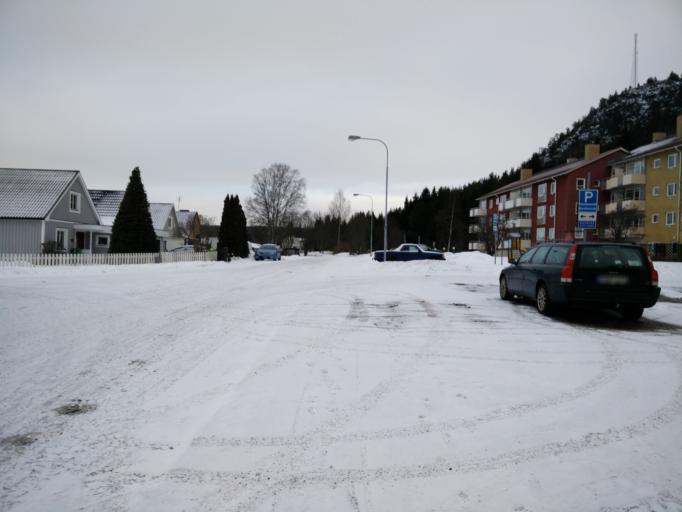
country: SE
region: Vaesternorrland
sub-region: Sundsvalls Kommun
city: Kvissleby
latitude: 62.2956
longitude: 17.3693
